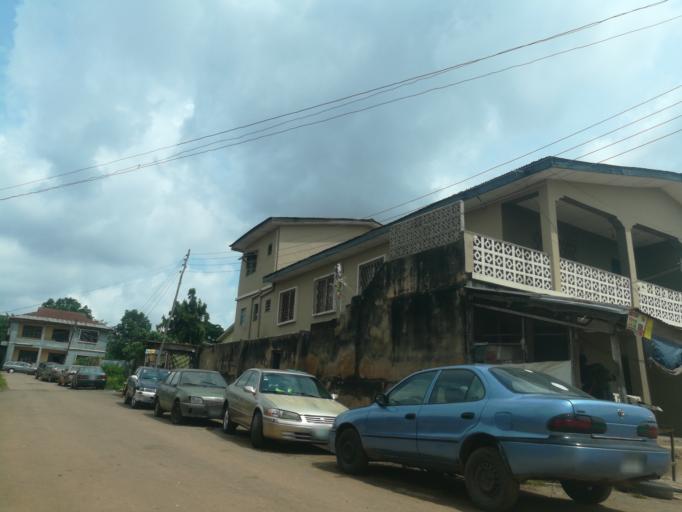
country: NG
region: Oyo
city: Ibadan
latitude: 7.3594
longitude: 3.8824
